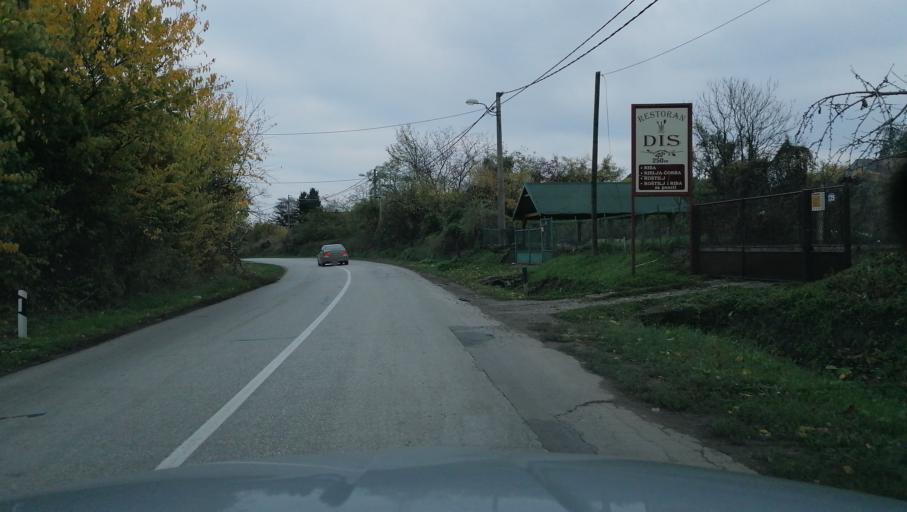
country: RS
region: Central Serbia
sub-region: Podunavski Okrug
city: Smederevo
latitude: 44.6569
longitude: 20.8729
